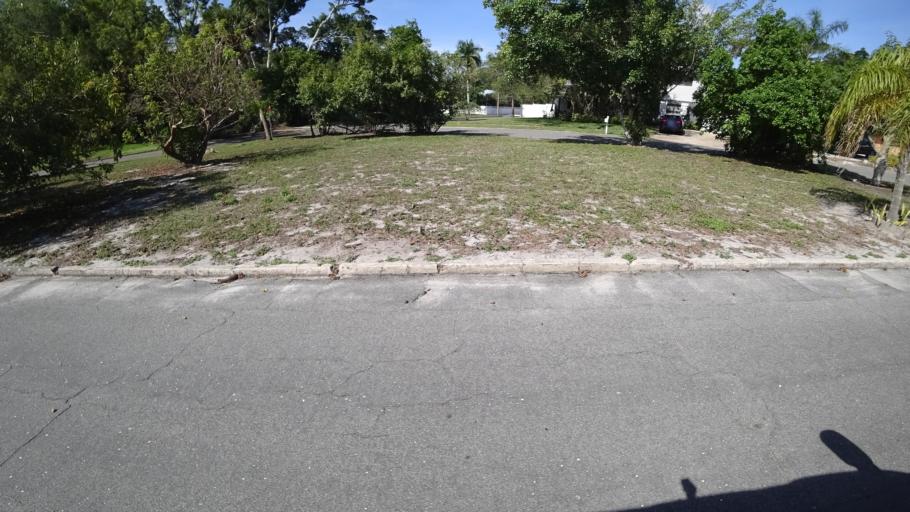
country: US
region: Florida
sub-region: Manatee County
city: West Bradenton
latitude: 27.5059
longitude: -82.6169
